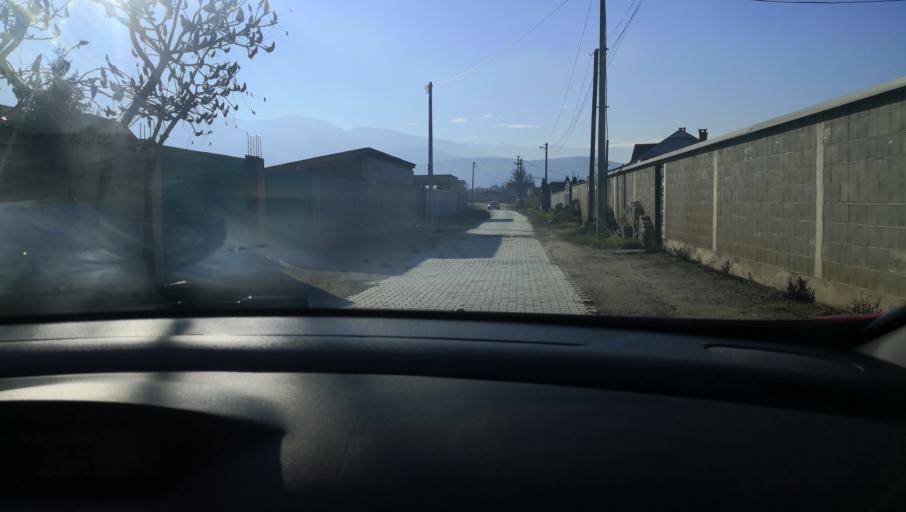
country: MK
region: Brvenica
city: Celopek
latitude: 41.9333
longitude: 21.0060
